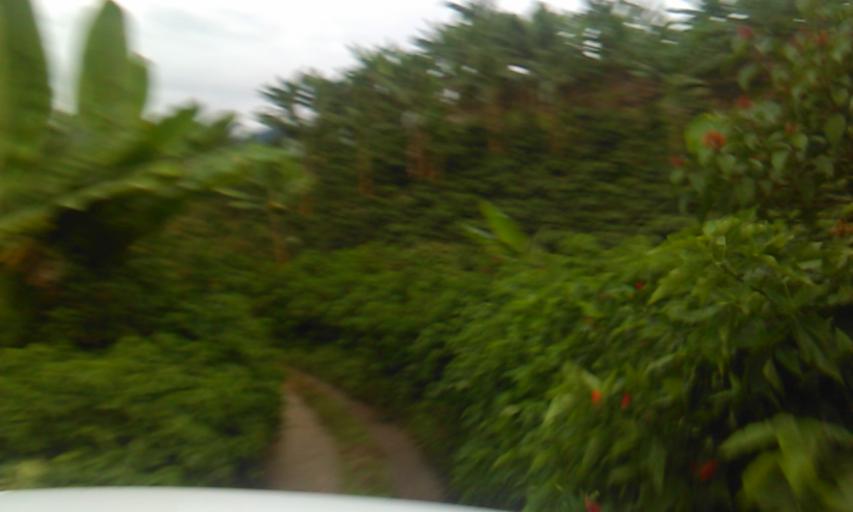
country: CO
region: Quindio
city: Cordoba
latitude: 4.4102
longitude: -75.6838
